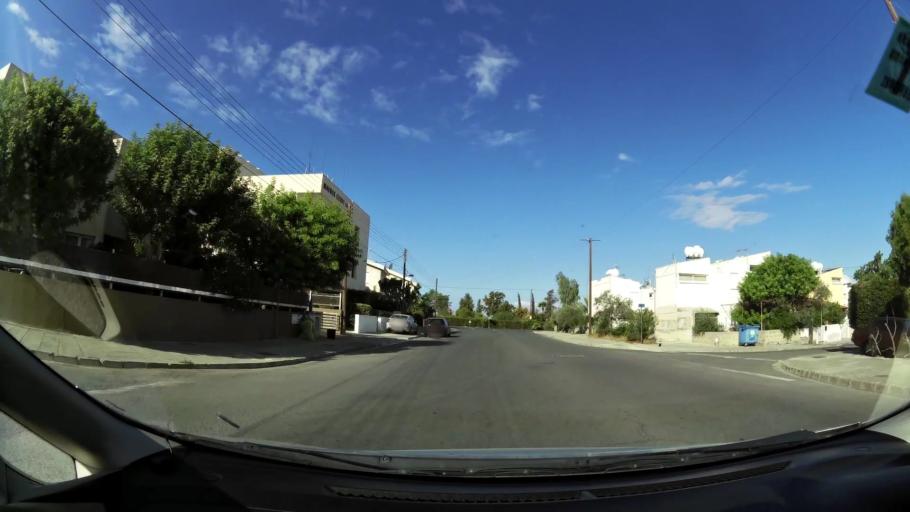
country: CY
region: Lefkosia
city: Nicosia
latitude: 35.1245
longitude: 33.3449
